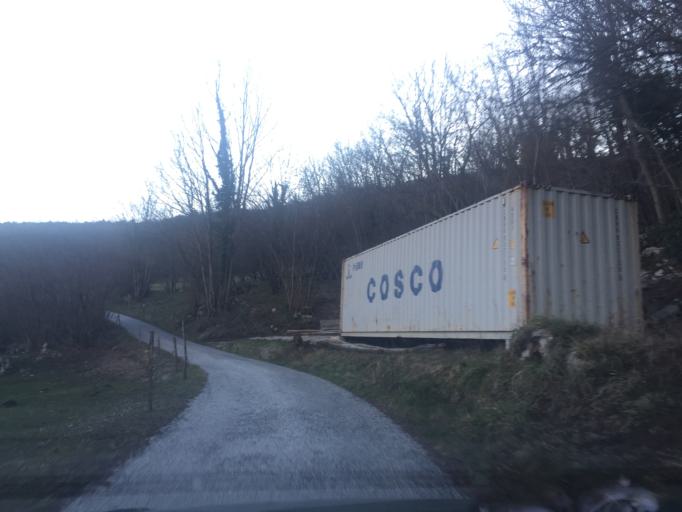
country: SI
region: Kanal
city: Deskle
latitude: 46.0427
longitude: 13.6629
